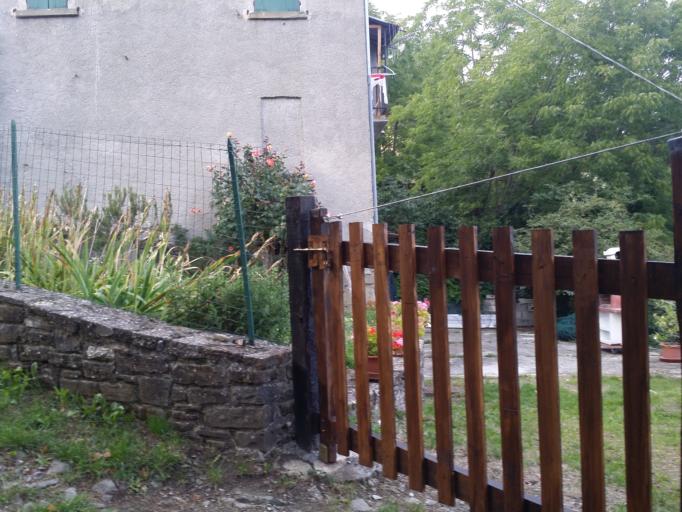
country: IT
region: Emilia-Romagna
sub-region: Provincia di Parma
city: Borgo Val di Taro
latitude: 44.5307
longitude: 9.7930
